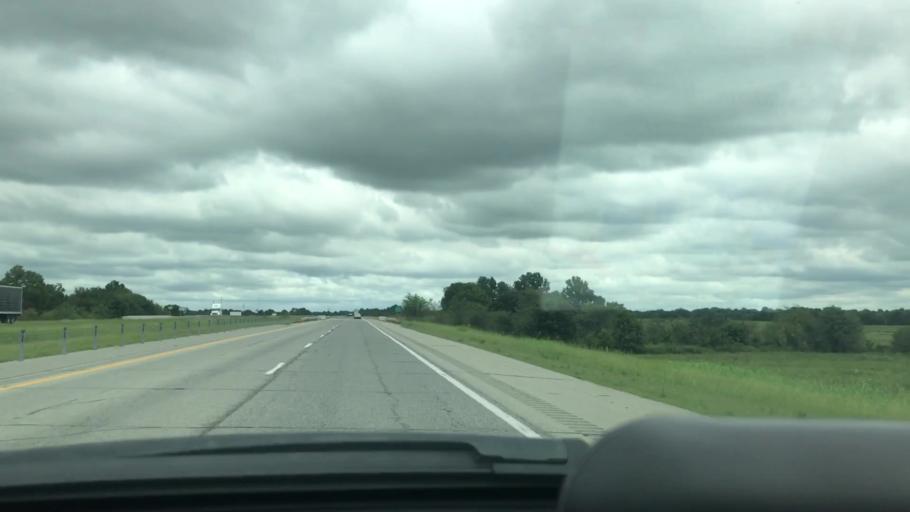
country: US
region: Oklahoma
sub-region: McIntosh County
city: Checotah
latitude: 35.5494
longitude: -95.4995
